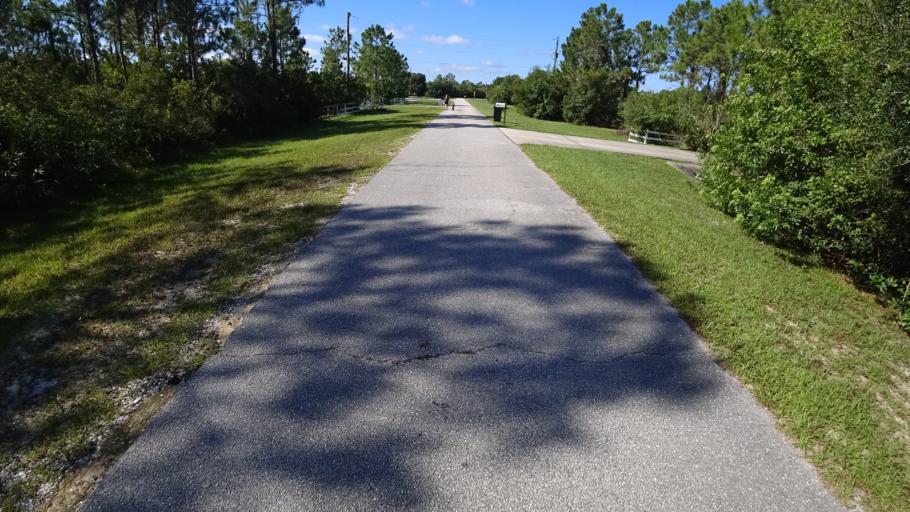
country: US
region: Florida
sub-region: Sarasota County
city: The Meadows
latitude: 27.4254
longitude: -82.3489
